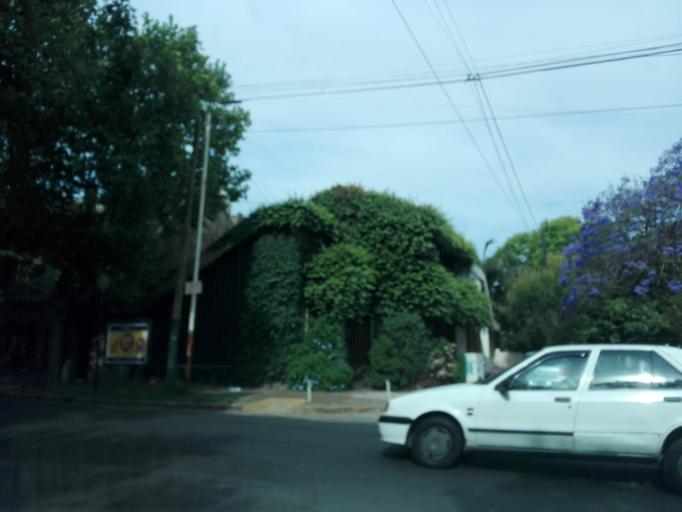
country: AR
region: Buenos Aires
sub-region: Partido de Lomas de Zamora
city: Lomas de Zamora
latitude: -34.7526
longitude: -58.3980
